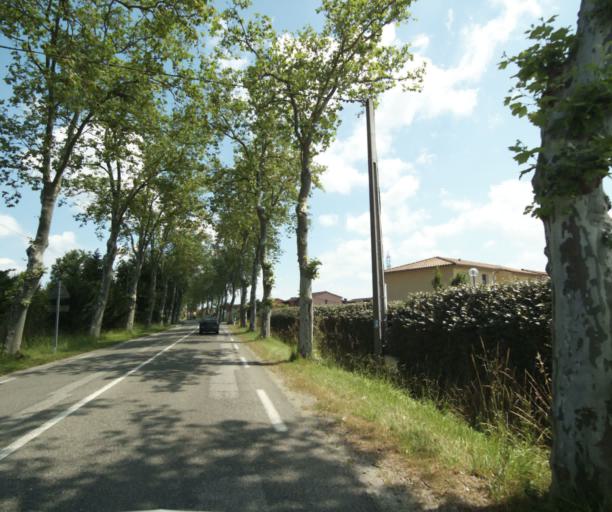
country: FR
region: Midi-Pyrenees
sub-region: Departement du Tarn-et-Garonne
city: Montauban
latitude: 44.0470
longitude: 1.3573
